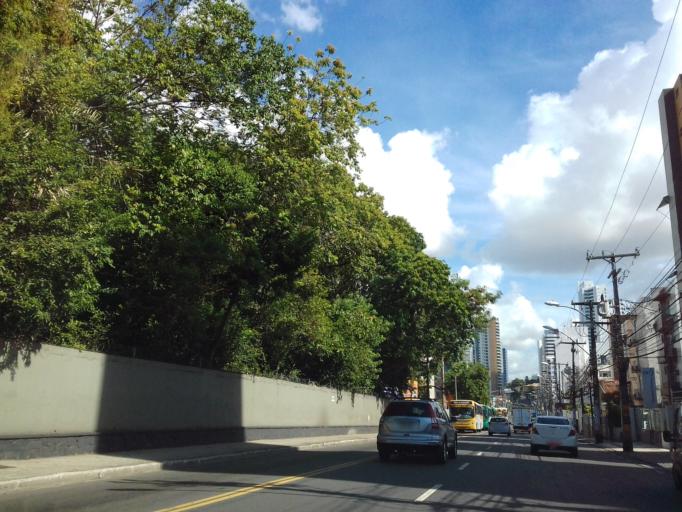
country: BR
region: Bahia
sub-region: Salvador
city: Salvador
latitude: -12.9949
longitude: -38.4547
